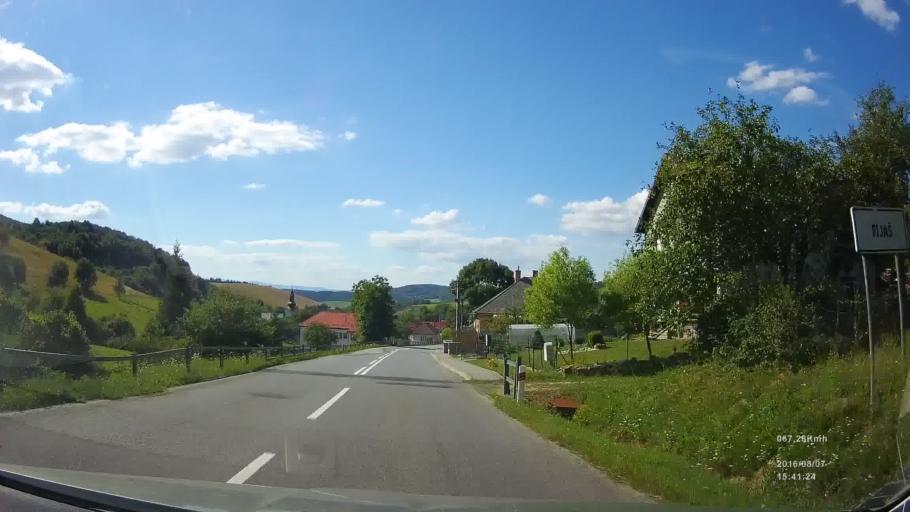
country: SK
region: Presovsky
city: Giraltovce
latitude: 49.1244
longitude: 21.5784
